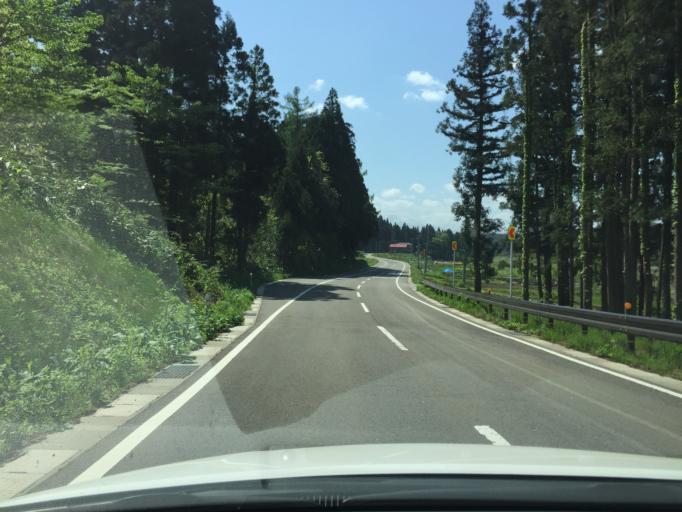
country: JP
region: Niigata
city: Kamo
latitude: 37.5712
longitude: 139.0836
